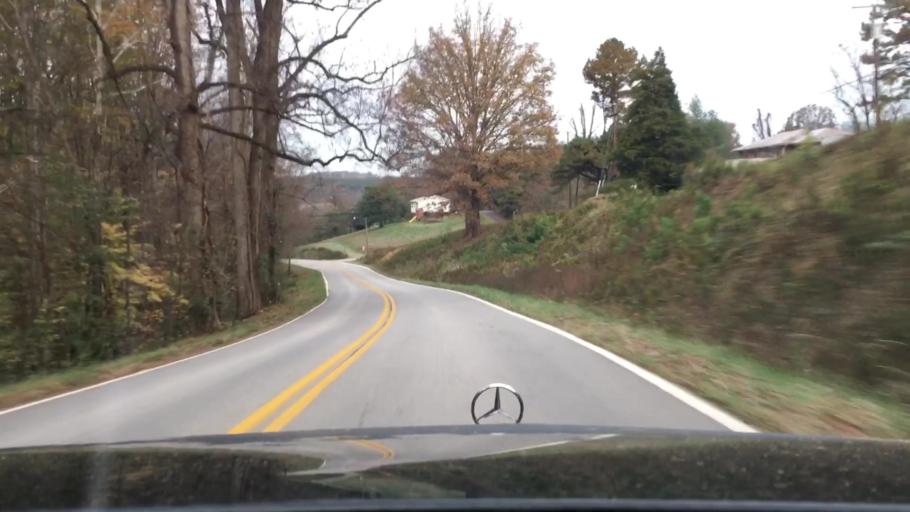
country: US
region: Virginia
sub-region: Pittsylvania County
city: Hurt
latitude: 37.0997
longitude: -79.2962
